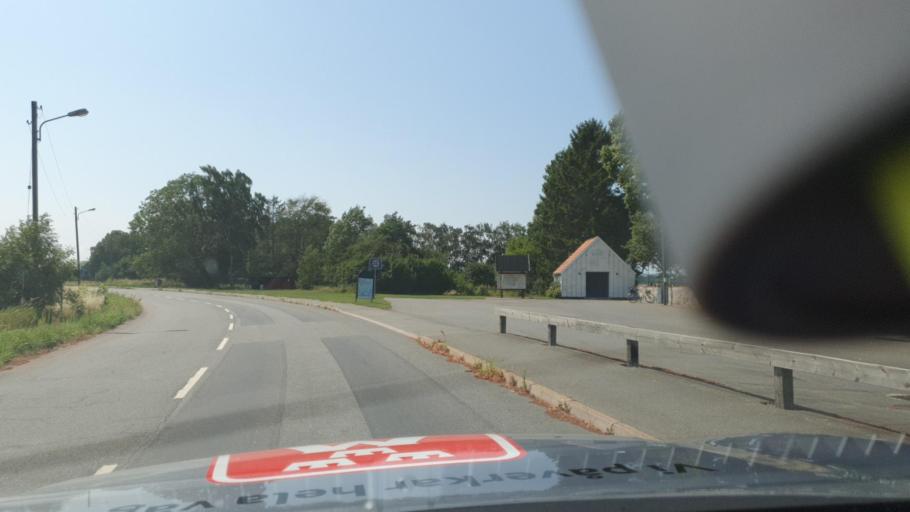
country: SE
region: Skane
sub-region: Bromolla Kommun
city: Bromoella
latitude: 56.0479
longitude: 14.4087
